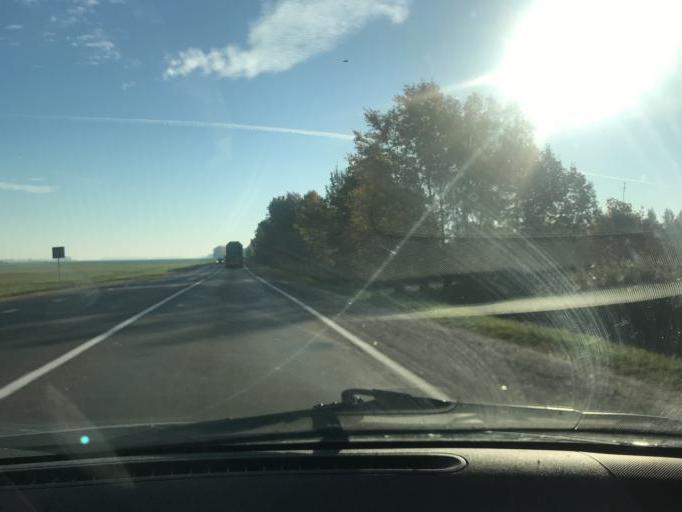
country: BY
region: Brest
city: Ivanava
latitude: 52.1517
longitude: 25.3726
